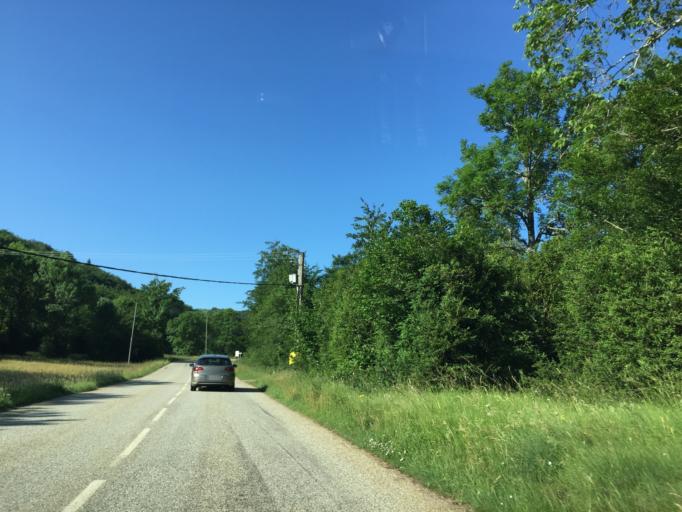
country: FR
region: Rhone-Alpes
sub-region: Departement de la Drome
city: Saint-Laurent-en-Royans
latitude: 44.9484
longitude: 5.3958
